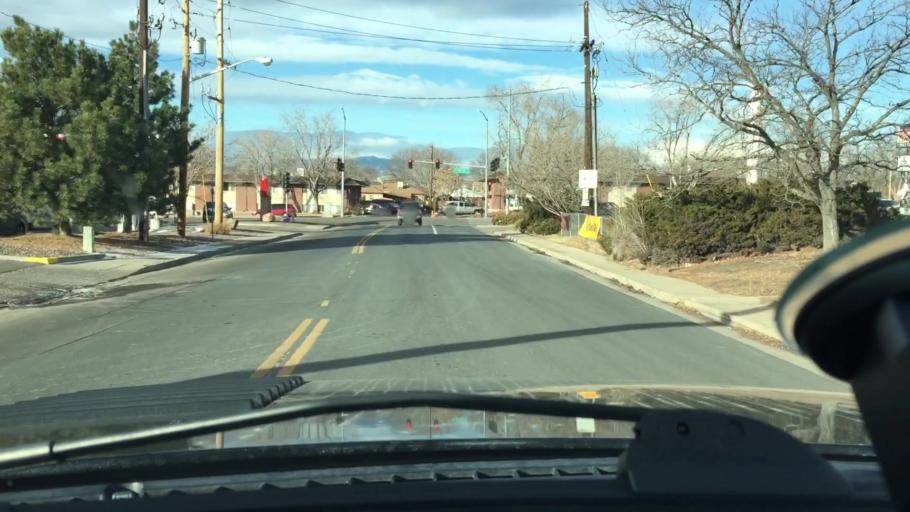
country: US
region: Colorado
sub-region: Adams County
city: Sherrelwood
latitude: 39.8325
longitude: -105.0050
